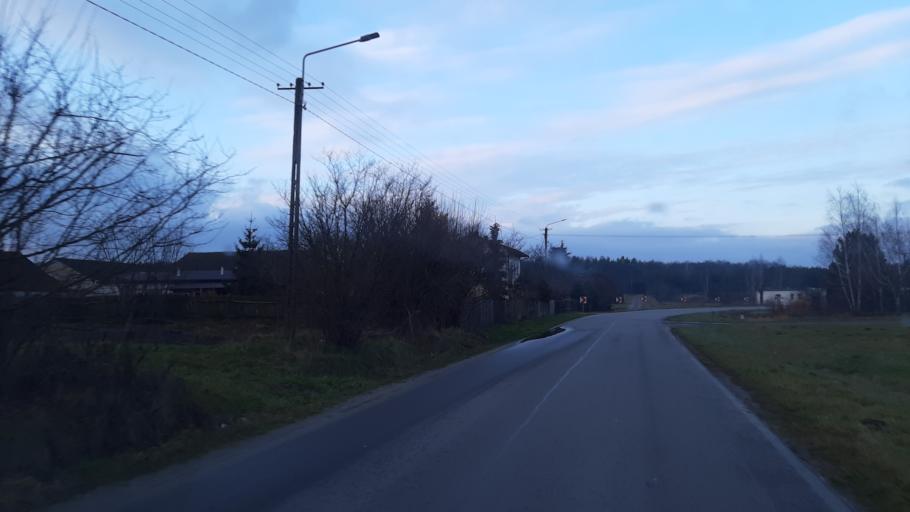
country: PL
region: Lublin Voivodeship
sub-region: Powiat lubelski
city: Garbow
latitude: 51.3936
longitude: 22.4095
